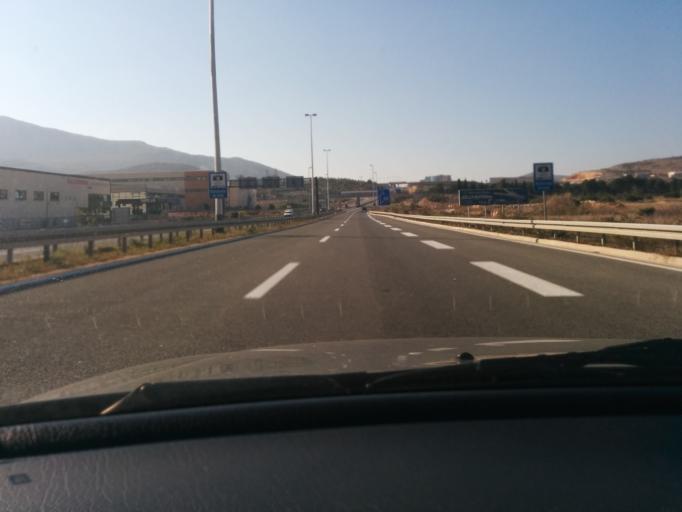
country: HR
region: Splitsko-Dalmatinska
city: Dugopolje
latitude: 43.5901
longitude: 16.5709
